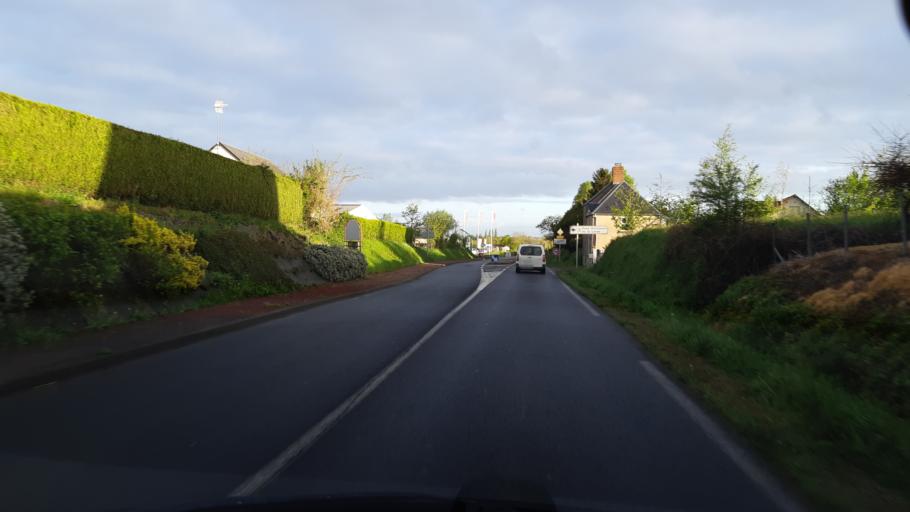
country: FR
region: Lower Normandy
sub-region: Departement de la Manche
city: Agneaux
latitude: 49.0515
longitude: -1.1293
